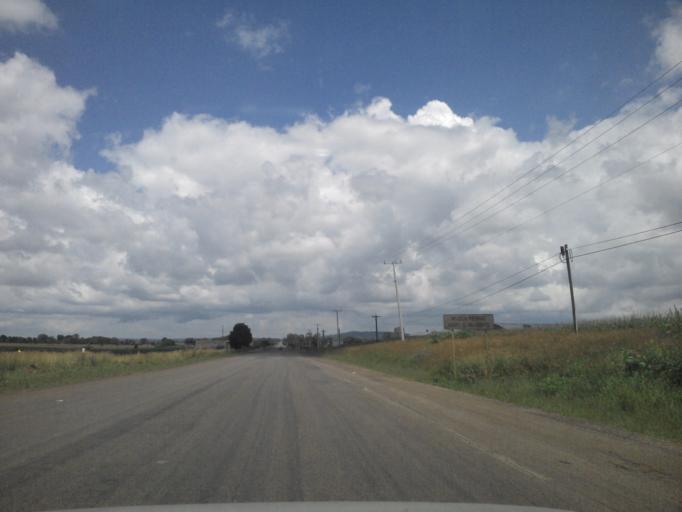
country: MX
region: Jalisco
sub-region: Atotonilco el Alto
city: Ojo de Agua de Moran
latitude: 20.5907
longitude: -102.4956
